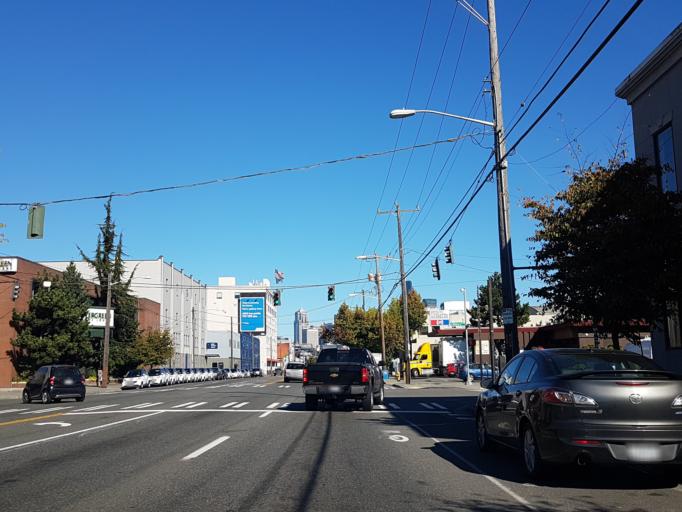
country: US
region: Washington
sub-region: King County
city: Seattle
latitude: 47.5816
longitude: -122.3341
